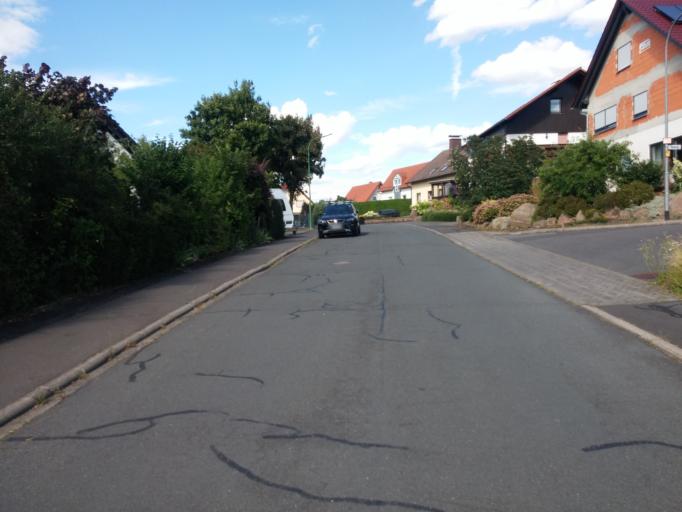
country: DE
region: Hesse
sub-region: Regierungsbezirk Kassel
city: Hunfeld
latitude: 50.6610
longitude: 9.7391
